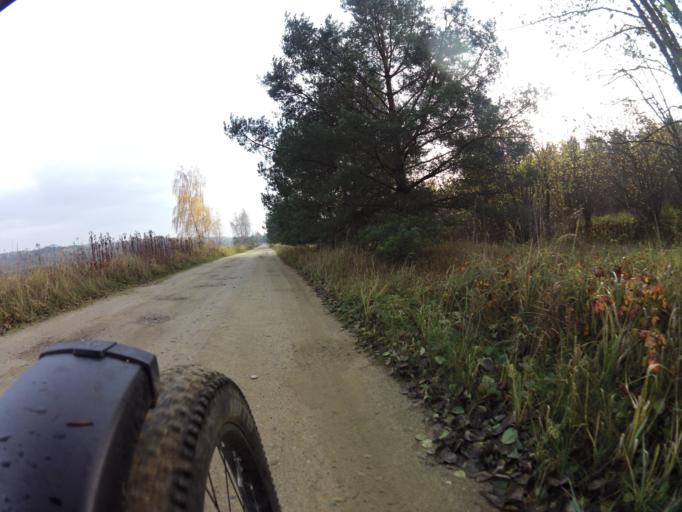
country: PL
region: Pomeranian Voivodeship
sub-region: Powiat wejherowski
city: Orle
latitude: 54.7018
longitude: 18.1091
